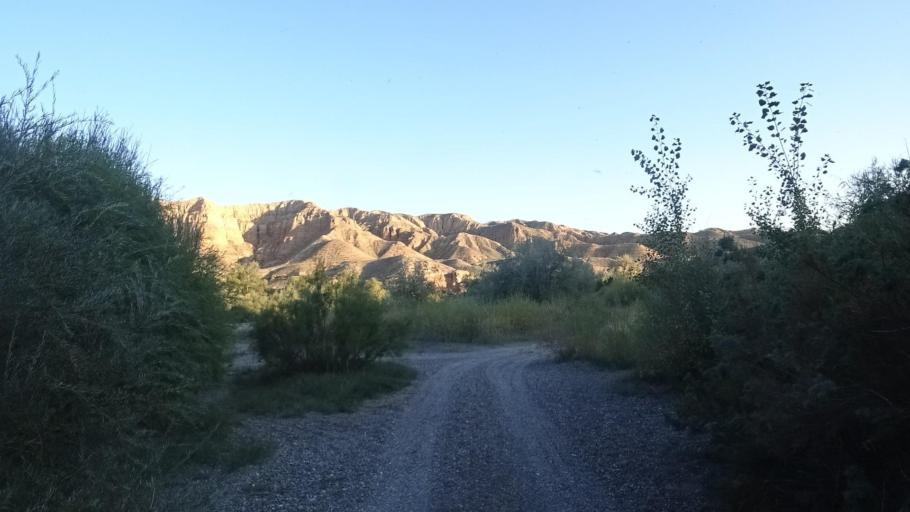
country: KZ
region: Almaty Oblysy
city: Kegen
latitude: 43.2739
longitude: 78.9770
